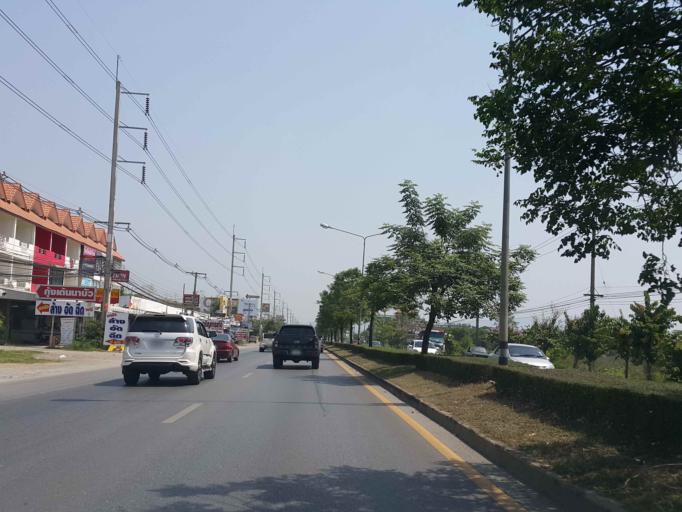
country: TH
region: Chiang Mai
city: San Sai
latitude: 18.8619
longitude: 99.0148
